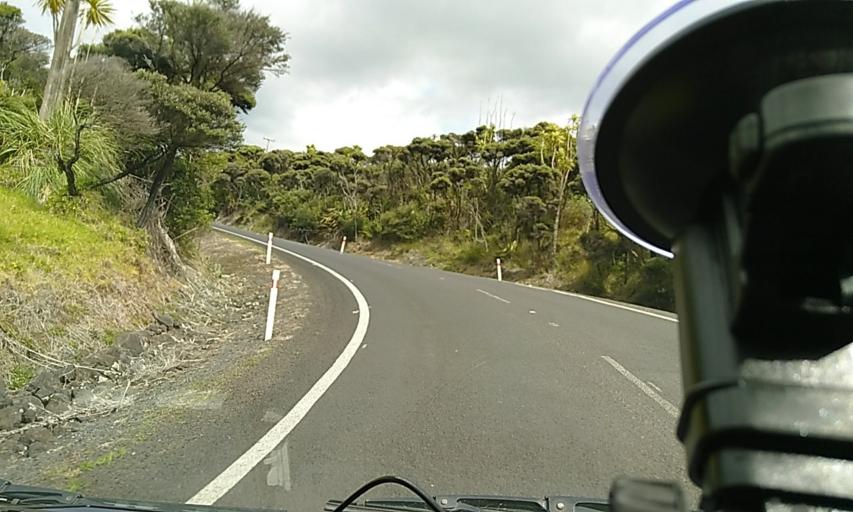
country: NZ
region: Northland
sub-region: Far North District
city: Ahipara
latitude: -35.5401
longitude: 173.3849
